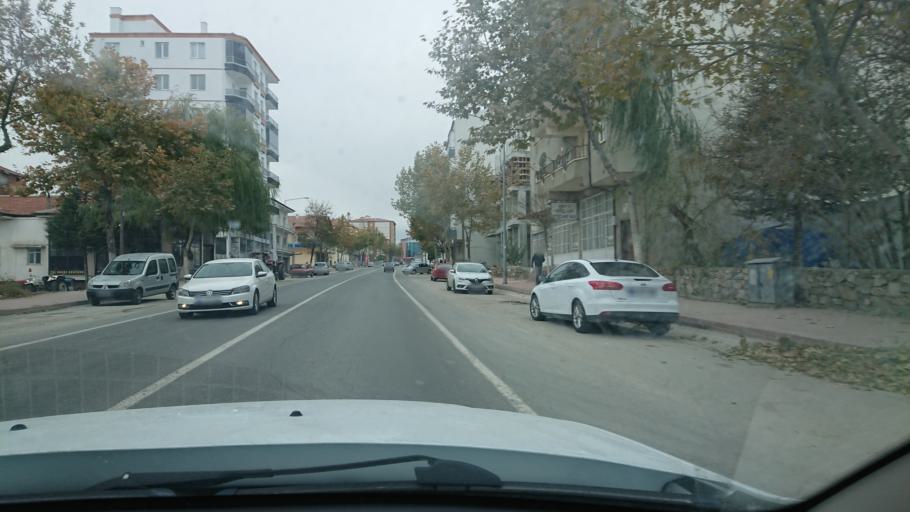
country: TR
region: Aksaray
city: Ortakoy
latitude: 38.7412
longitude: 34.0452
